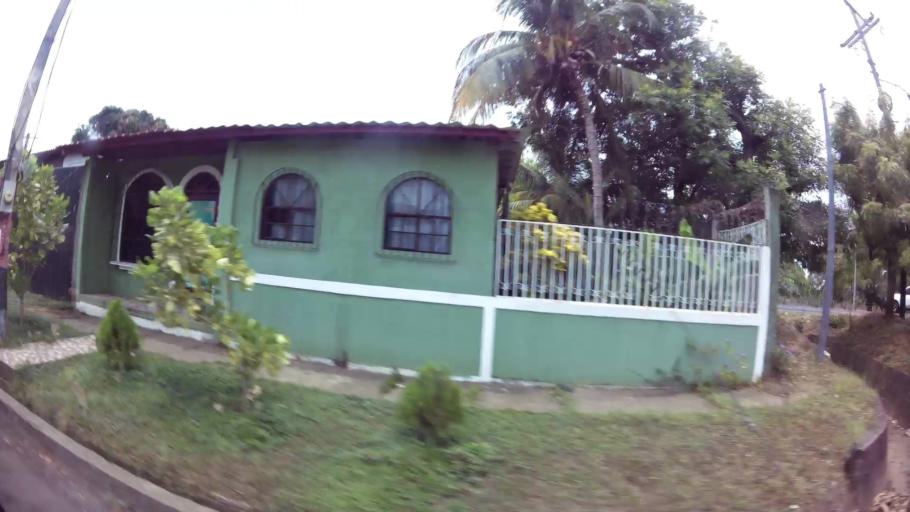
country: NI
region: Leon
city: Leon
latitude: 12.4175
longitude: -86.8686
